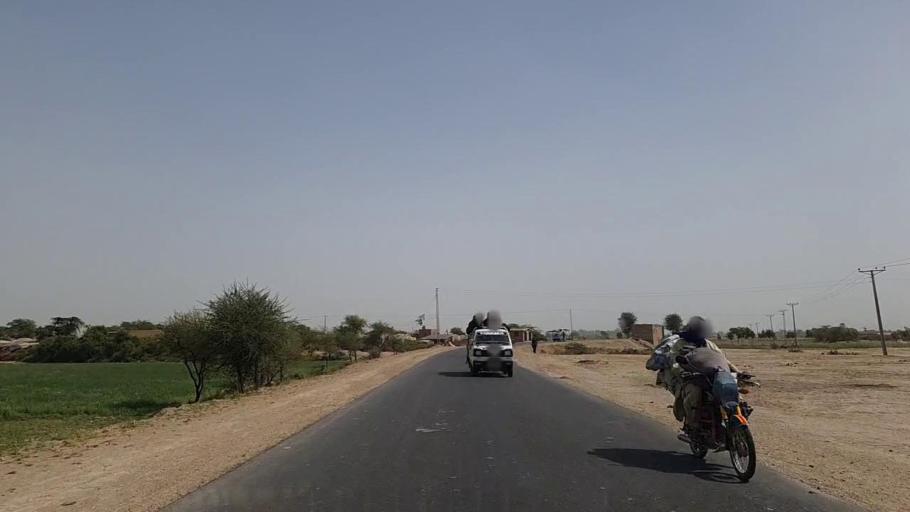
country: PK
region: Sindh
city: Talhar
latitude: 24.8446
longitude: 68.8844
